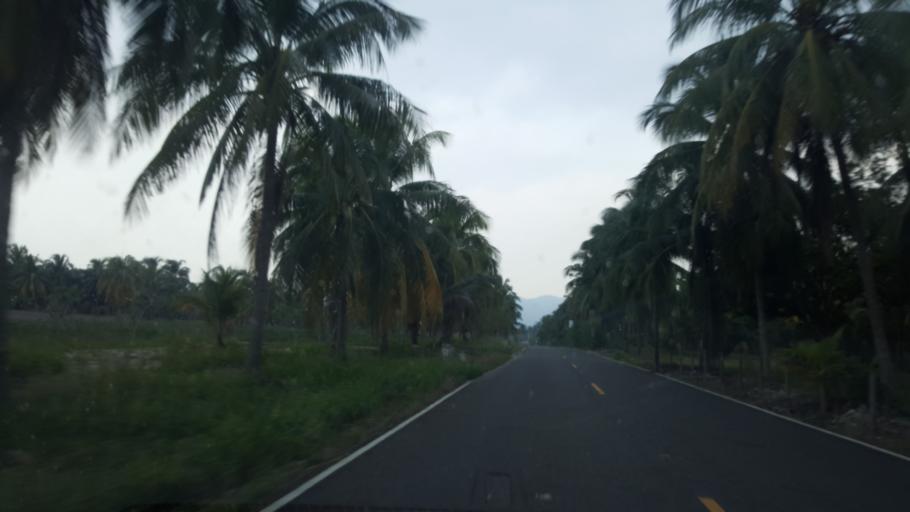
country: TH
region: Chon Buri
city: Ban Bueng
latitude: 13.2289
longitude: 101.0352
